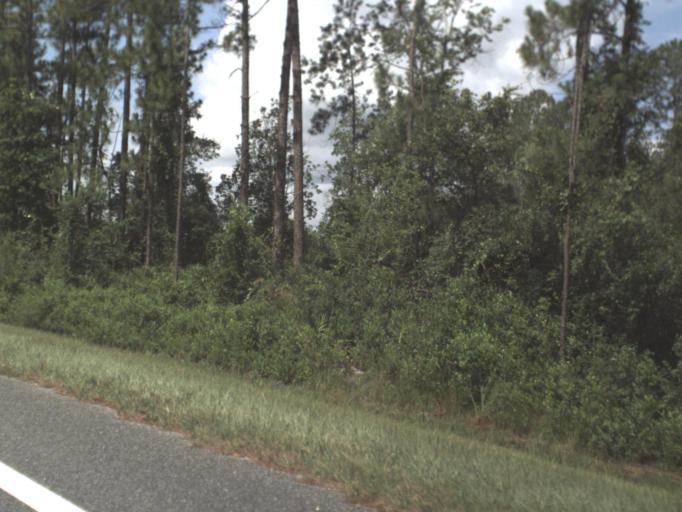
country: US
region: Florida
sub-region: Union County
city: Lake Butler
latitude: 30.1120
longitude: -82.2165
